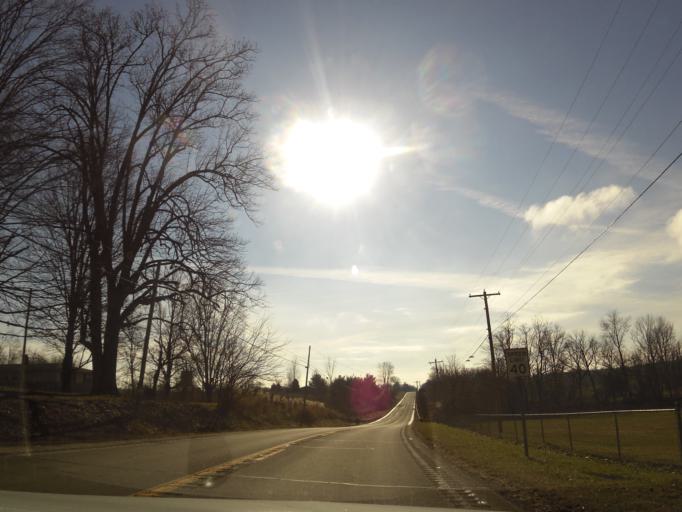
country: US
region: Indiana
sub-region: Jennings County
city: North Vernon
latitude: 38.8883
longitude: -85.5189
